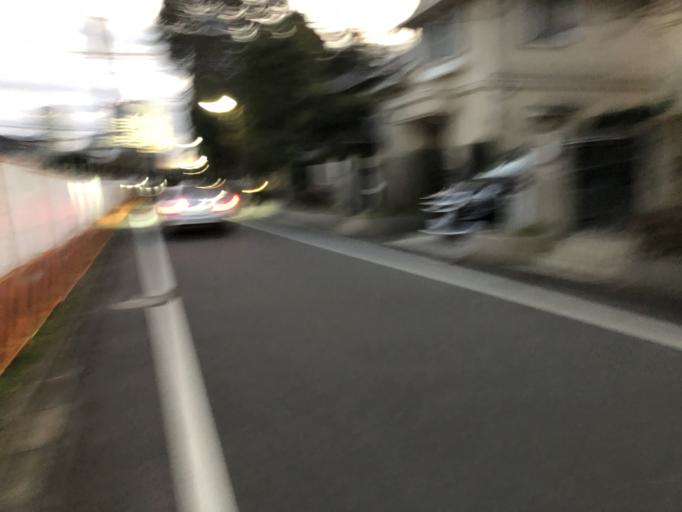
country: JP
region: Tokyo
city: Chofugaoka
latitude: 35.6175
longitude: 139.6301
